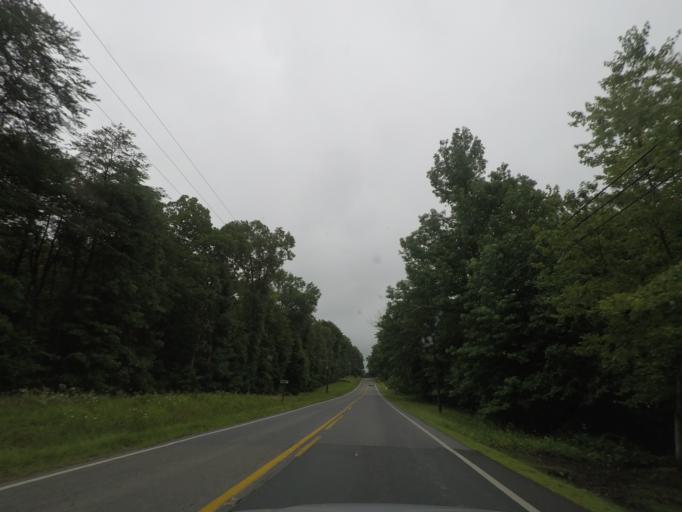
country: US
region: Virginia
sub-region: Fluvanna County
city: Weber City
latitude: 37.7781
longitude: -78.2448
